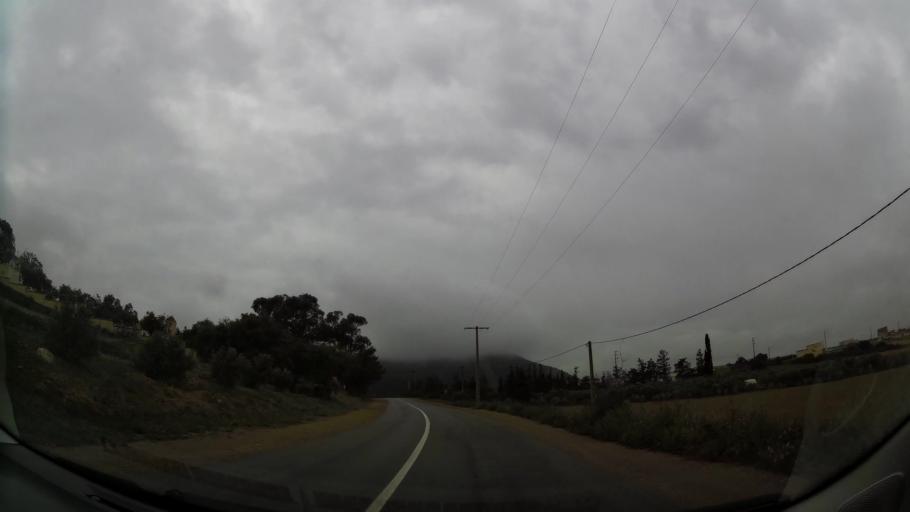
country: MA
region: Oriental
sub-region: Nador
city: Nador
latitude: 35.1392
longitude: -3.0500
